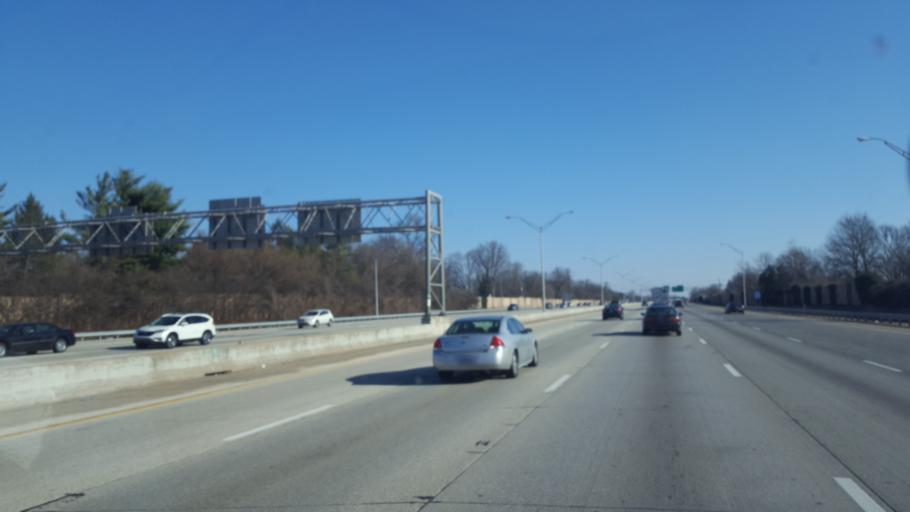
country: US
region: Kentucky
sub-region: Jefferson County
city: West Buechel
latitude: 38.2131
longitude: -85.6674
